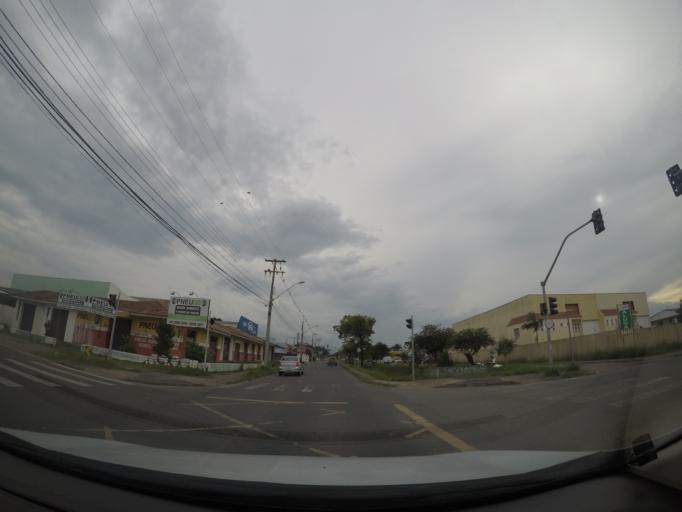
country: BR
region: Parana
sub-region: Sao Jose Dos Pinhais
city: Sao Jose dos Pinhais
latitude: -25.4948
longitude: -49.2381
